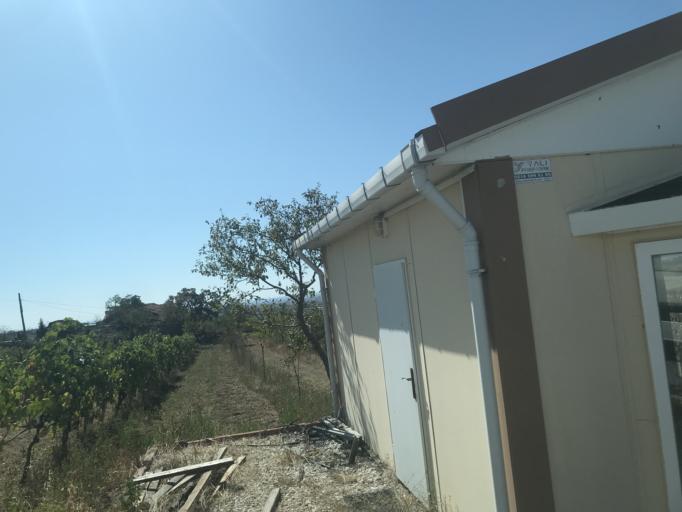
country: TR
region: Kirklareli
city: Kirklareli
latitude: 41.7878
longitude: 27.2342
